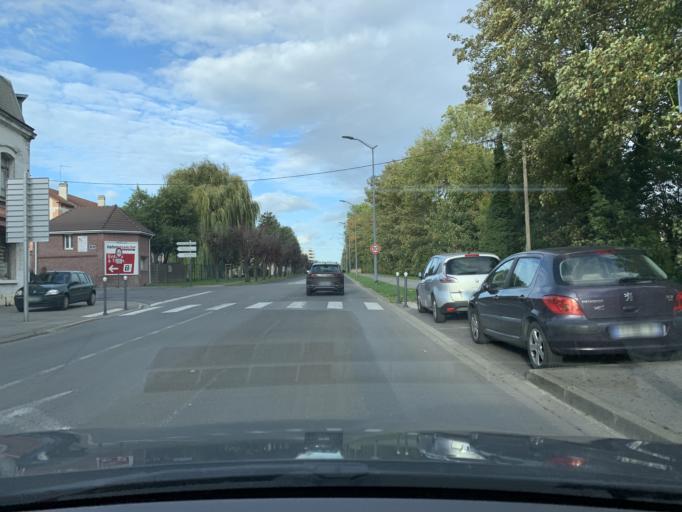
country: FR
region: Picardie
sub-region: Departement de l'Aisne
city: Harly
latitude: 49.8466
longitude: 3.3020
